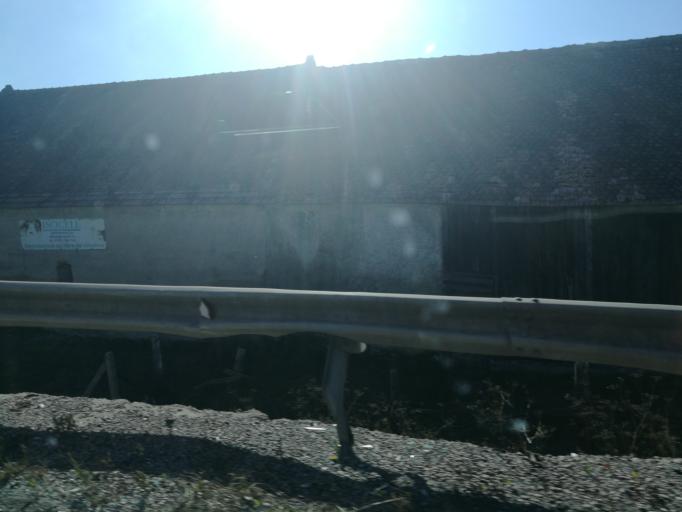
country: RO
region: Brasov
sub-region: Comuna Dumbravita
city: Dumbravita
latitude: 45.7684
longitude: 25.3628
